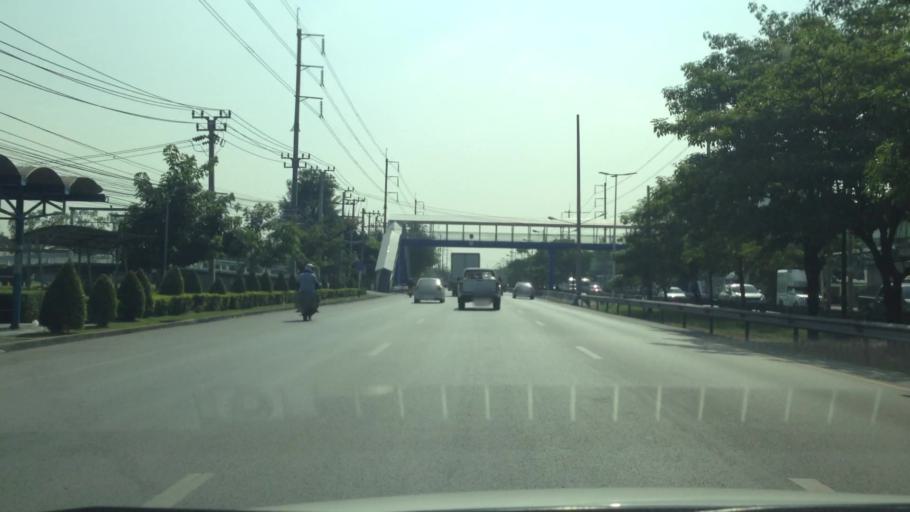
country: TH
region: Samut Prakan
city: Samut Prakan
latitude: 13.5317
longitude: 100.6315
